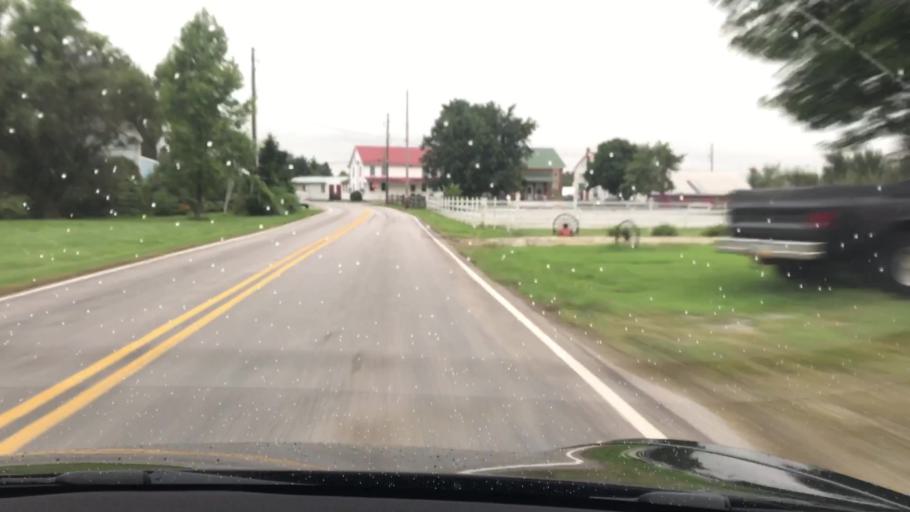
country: US
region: Pennsylvania
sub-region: York County
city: Dover
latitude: 39.9612
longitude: -76.8701
